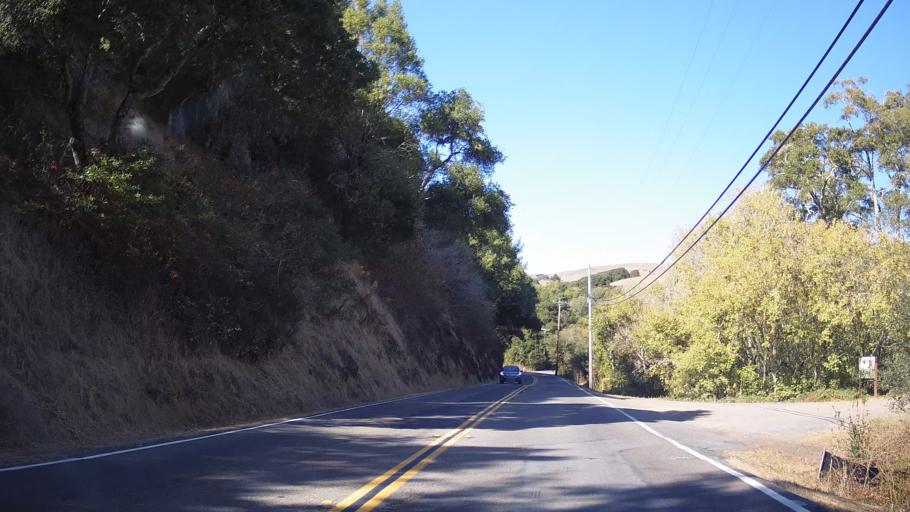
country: US
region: California
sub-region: Marin County
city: Inverness
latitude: 38.0795
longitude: -122.7845
